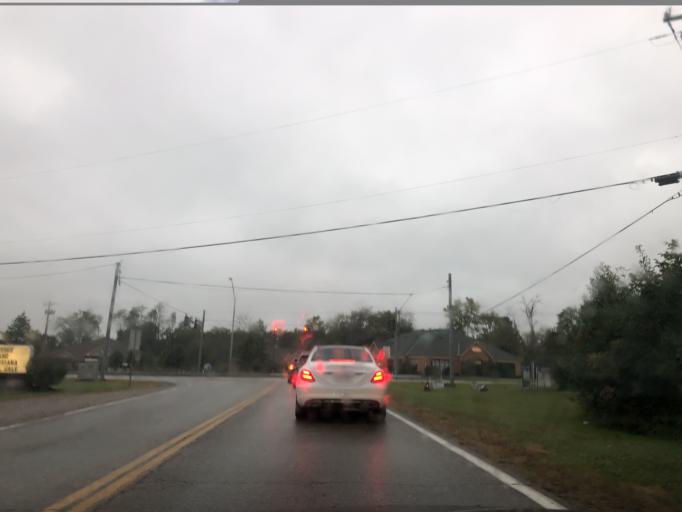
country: US
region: Ohio
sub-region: Hamilton County
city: The Village of Indian Hill
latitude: 39.2272
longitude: -84.2770
